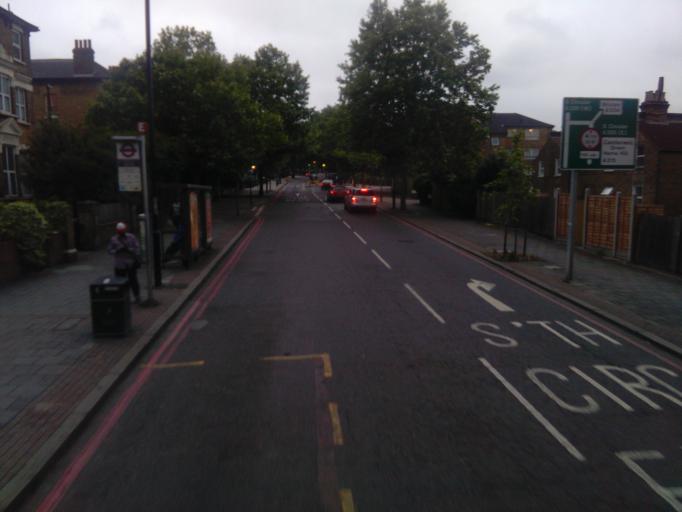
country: GB
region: England
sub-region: Greater London
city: Brixton Hill
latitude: 51.4404
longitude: -0.1073
